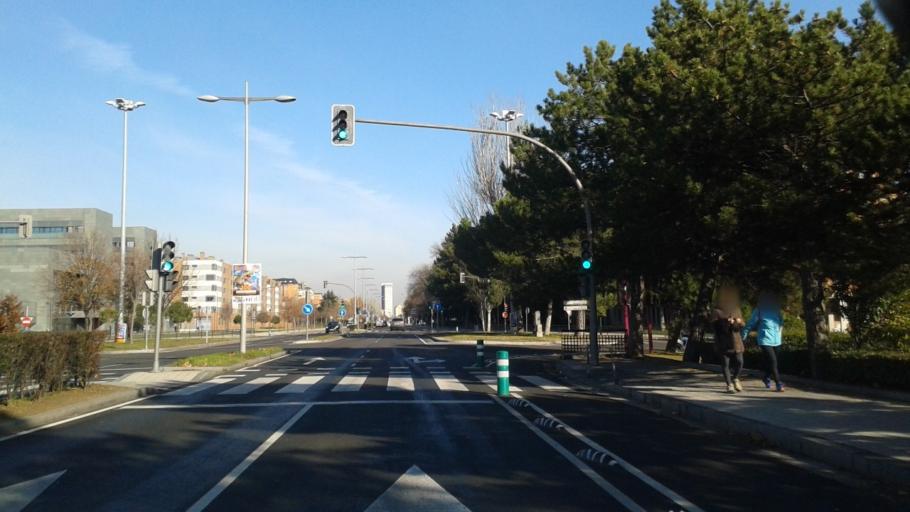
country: ES
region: Castille and Leon
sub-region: Provincia de Valladolid
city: Valladolid
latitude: 41.6439
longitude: -4.7433
